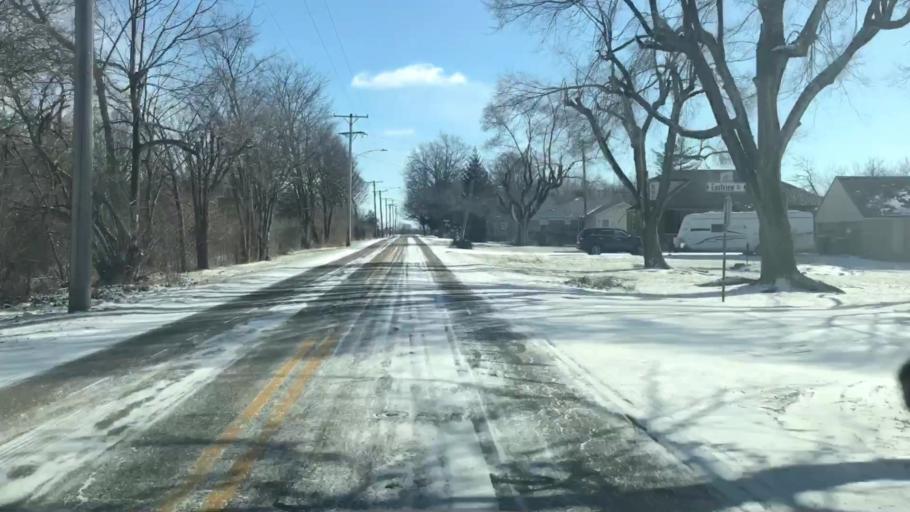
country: US
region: Ohio
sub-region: Greene County
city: Fairborn
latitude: 39.8405
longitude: -84.0104
